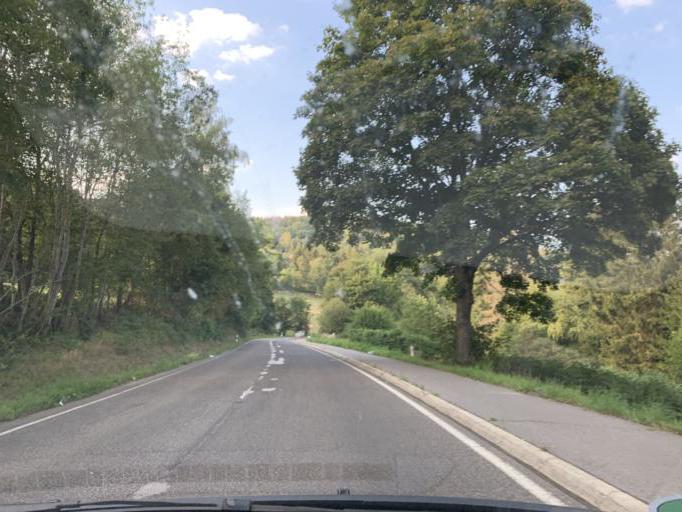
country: DE
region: North Rhine-Westphalia
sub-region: Regierungsbezirk Koln
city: Simmerath
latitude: 50.6200
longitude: 6.3749
